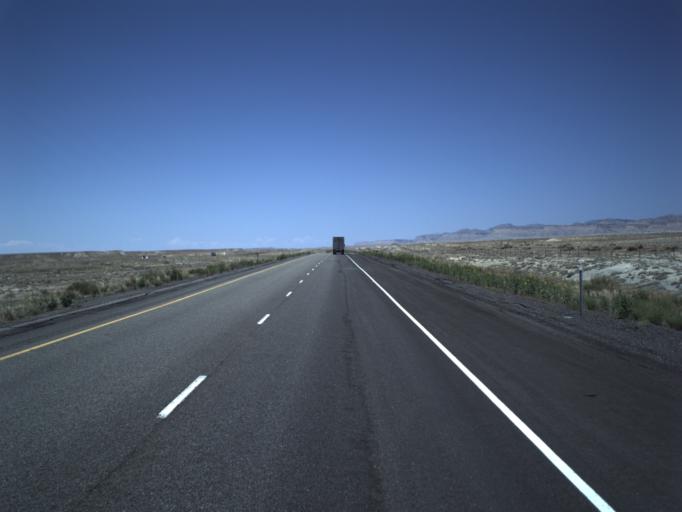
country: US
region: Utah
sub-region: Grand County
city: Moab
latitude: 38.9373
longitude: -109.4756
